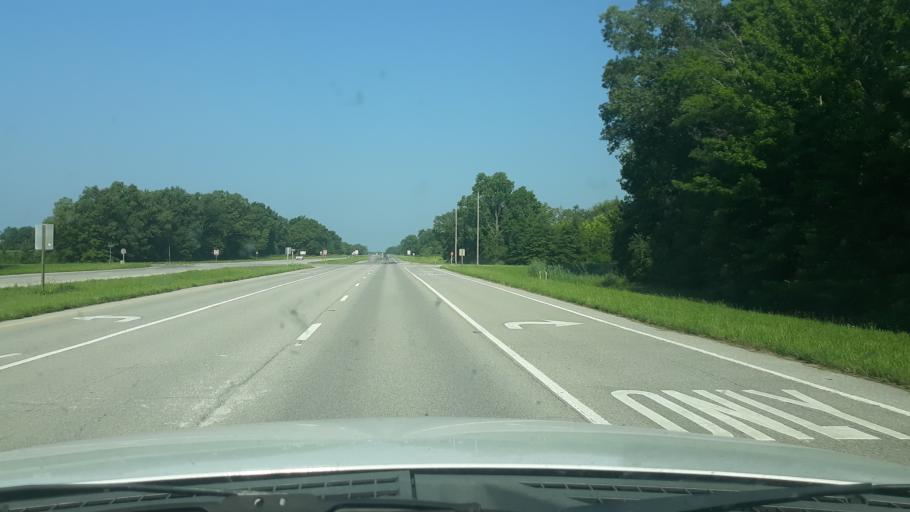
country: US
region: Illinois
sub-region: Saline County
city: Carrier Mills
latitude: 37.7336
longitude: -88.6323
